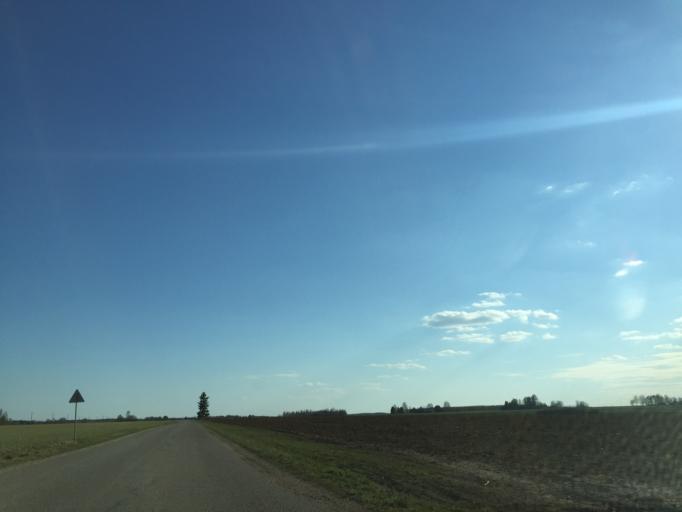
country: EE
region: Valgamaa
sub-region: Torva linn
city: Torva
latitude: 58.2245
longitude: 25.9155
